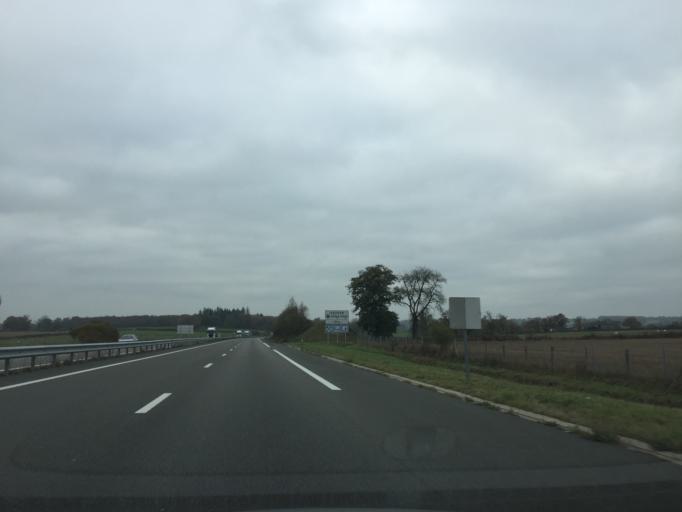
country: FR
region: Limousin
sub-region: Departement de la Creuse
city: Chambon-sur-Voueize
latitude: 46.2514
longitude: 2.3537
